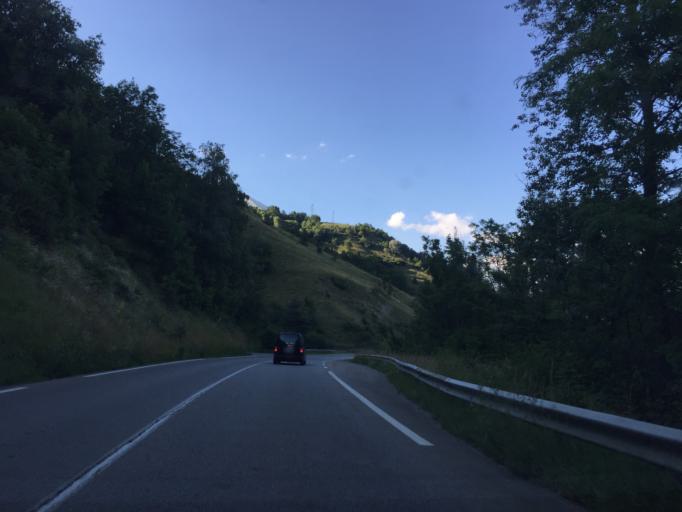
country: FR
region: Rhone-Alpes
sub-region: Departement de la Savoie
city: Bourg-Saint-Maurice
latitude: 45.5990
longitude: 6.7518
